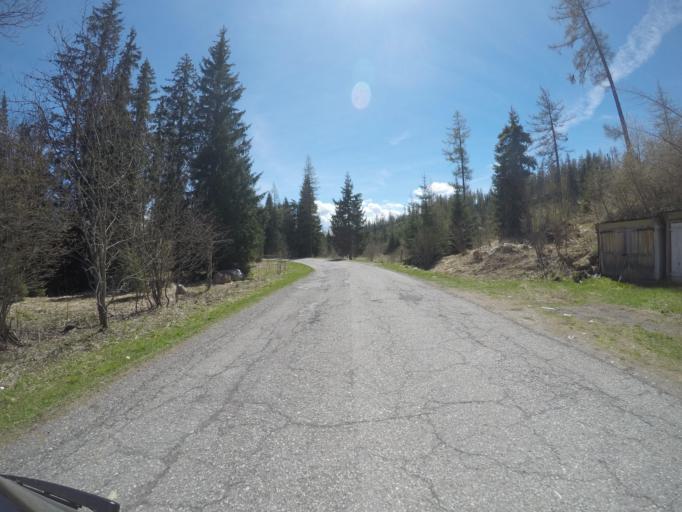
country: SK
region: Presovsky
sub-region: Okres Poprad
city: Strba
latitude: 49.1202
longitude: 20.0752
